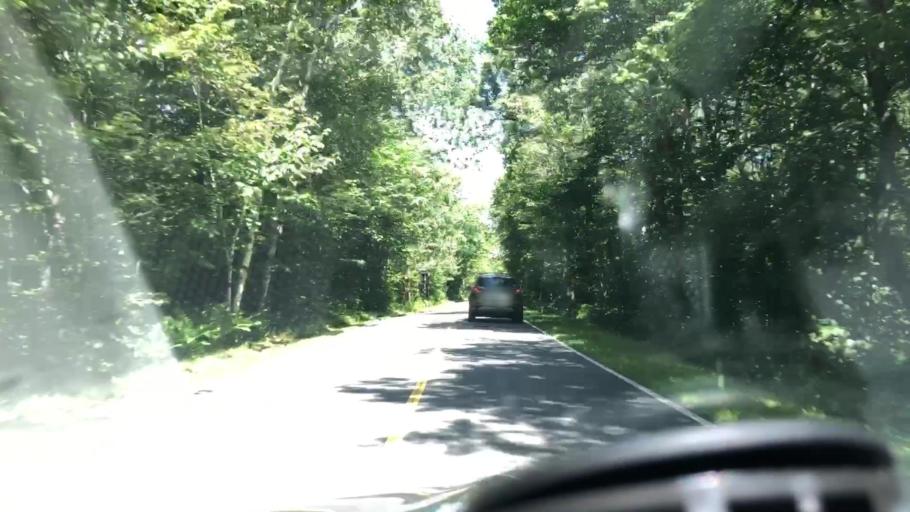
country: US
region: Massachusetts
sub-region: Berkshire County
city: Lanesborough
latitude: 42.5988
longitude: -73.2010
